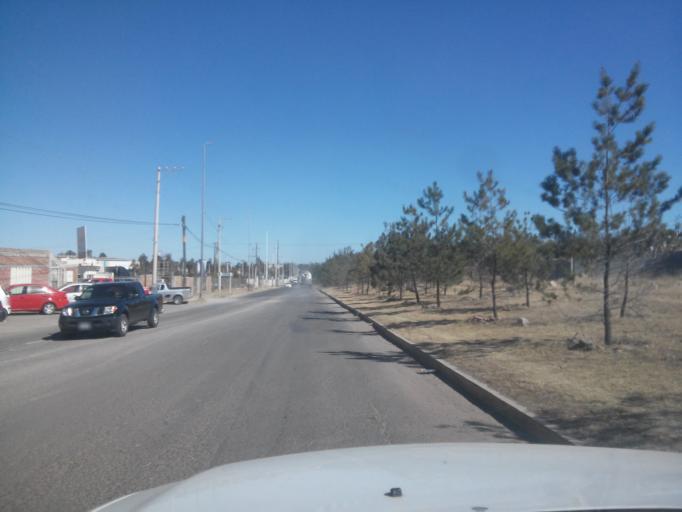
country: MX
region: Durango
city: Victoria de Durango
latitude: 24.0207
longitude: -104.7028
